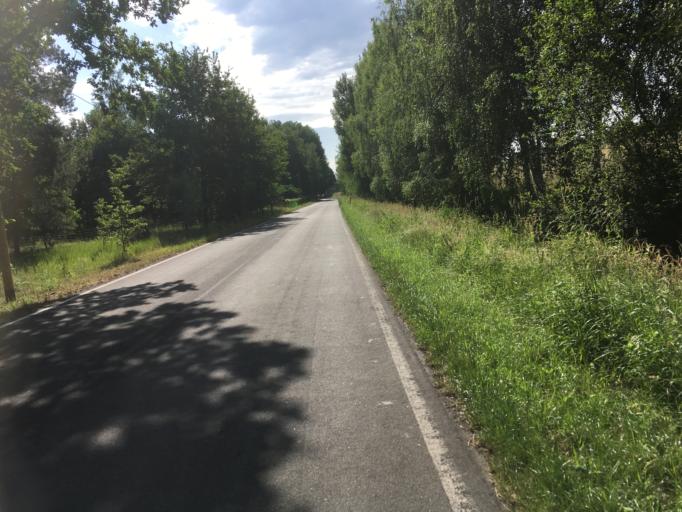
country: DE
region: Brandenburg
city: Drachhausen
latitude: 51.8518
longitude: 14.3131
